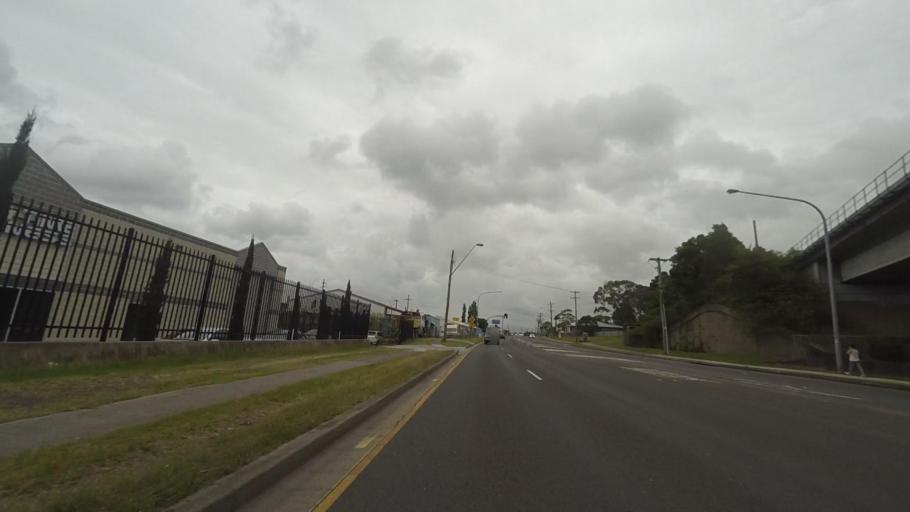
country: AU
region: New South Wales
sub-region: Wollongong
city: Cordeaux Heights
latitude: -34.4610
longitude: 150.8394
